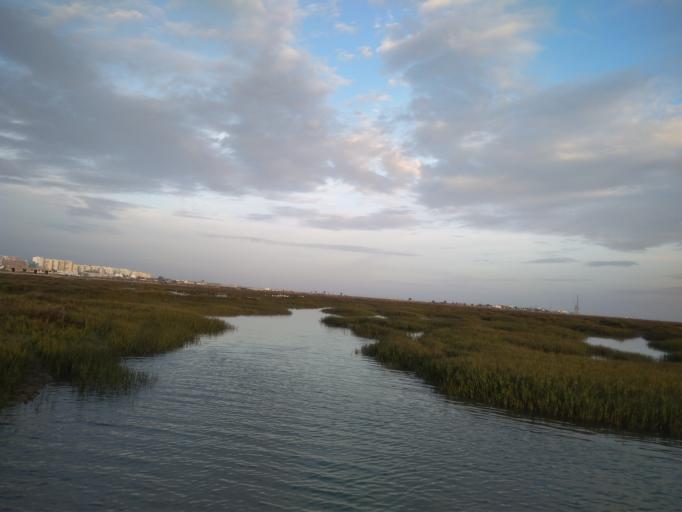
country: PT
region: Faro
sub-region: Faro
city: Faro
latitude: 37.0057
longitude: -7.9365
